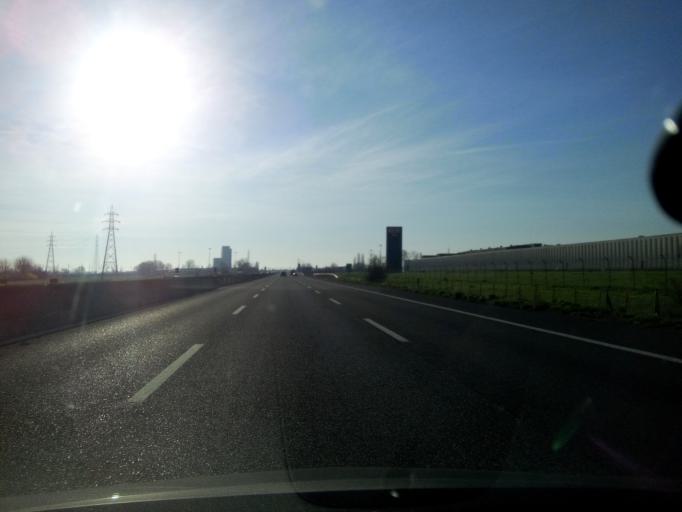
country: IT
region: Emilia-Romagna
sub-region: Provincia di Parma
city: Parma
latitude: 44.8299
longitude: 10.3701
